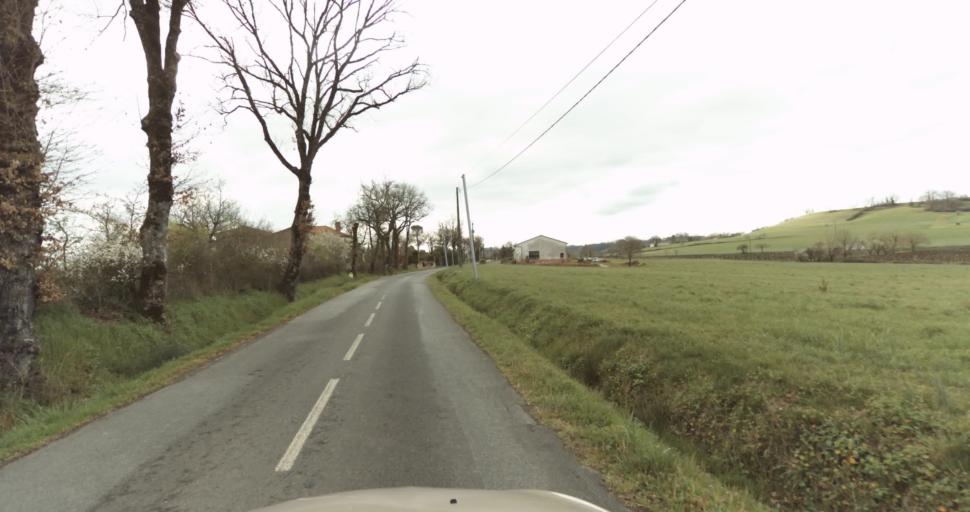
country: FR
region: Midi-Pyrenees
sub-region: Departement du Tarn
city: Puygouzon
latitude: 43.8913
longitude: 2.1915
